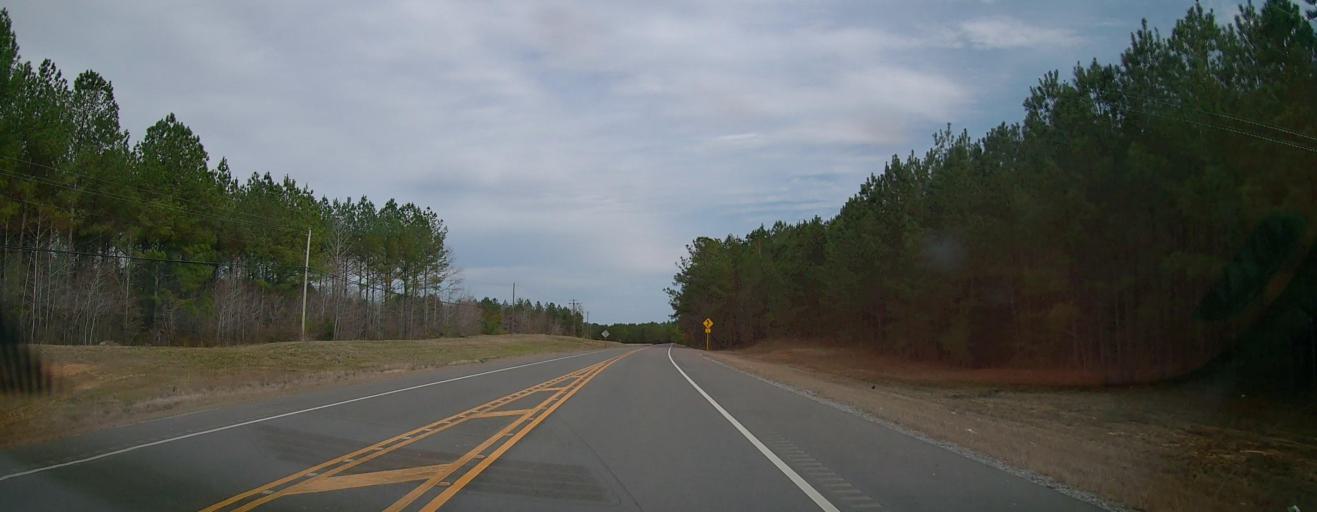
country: US
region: Alabama
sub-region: Walker County
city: Carbon Hill
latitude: 33.8668
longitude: -87.4225
